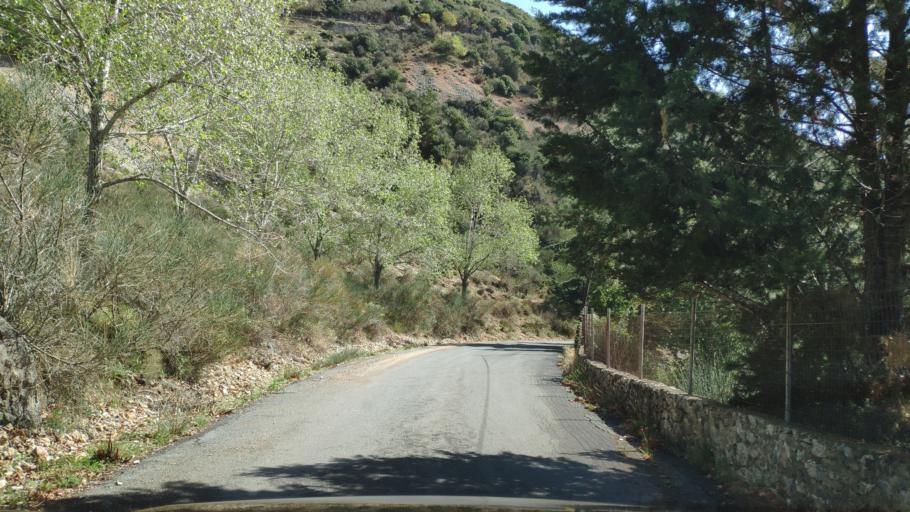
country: GR
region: Peloponnese
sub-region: Nomos Arkadias
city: Dimitsana
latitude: 37.5859
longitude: 22.0461
